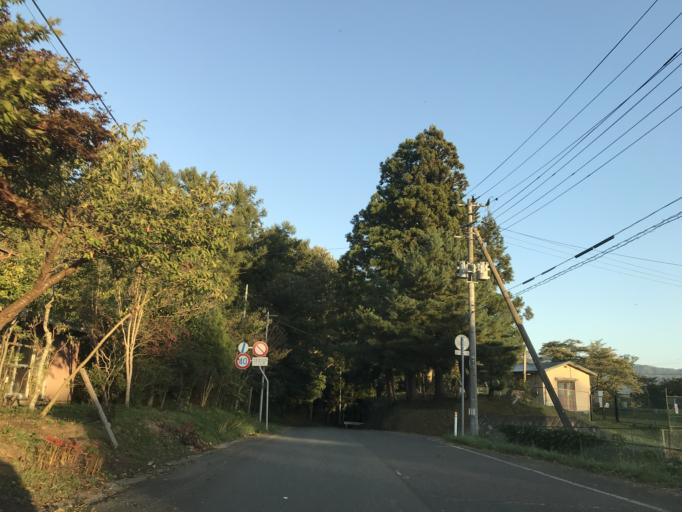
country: JP
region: Iwate
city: Mizusawa
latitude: 39.0515
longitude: 141.1186
